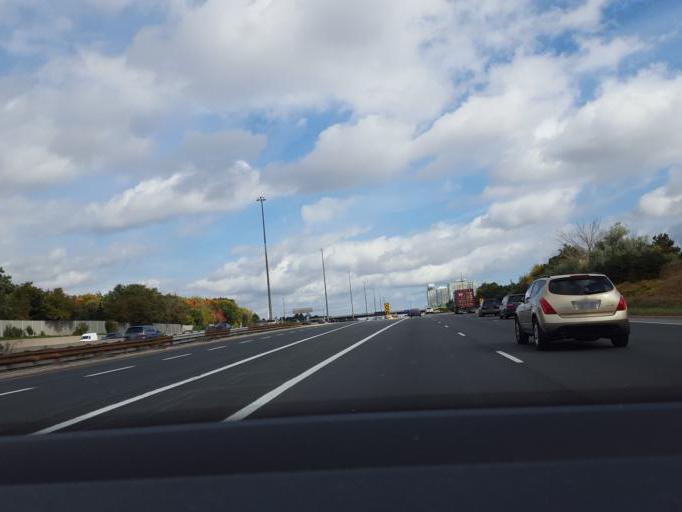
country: CA
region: Ontario
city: Scarborough
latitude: 43.7773
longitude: -79.2727
